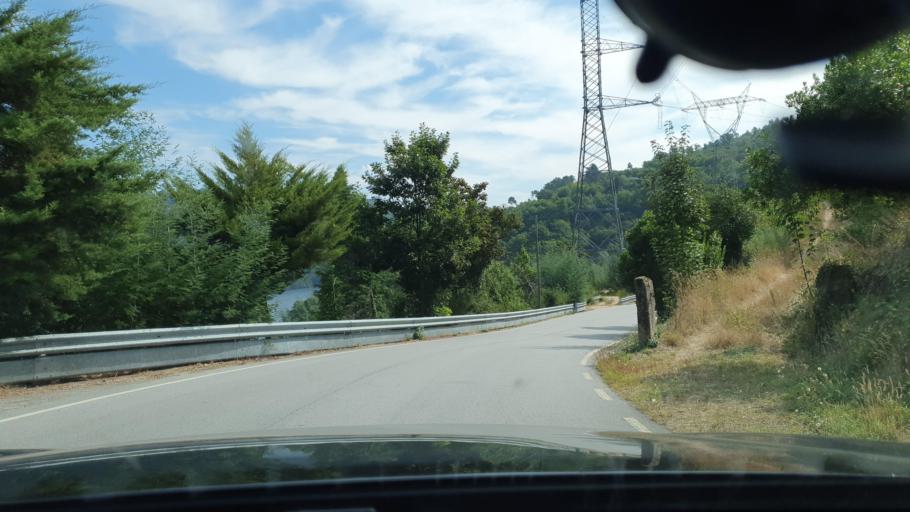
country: PT
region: Braga
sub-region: Vieira do Minho
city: Vieira do Minho
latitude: 41.6904
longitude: -8.0892
